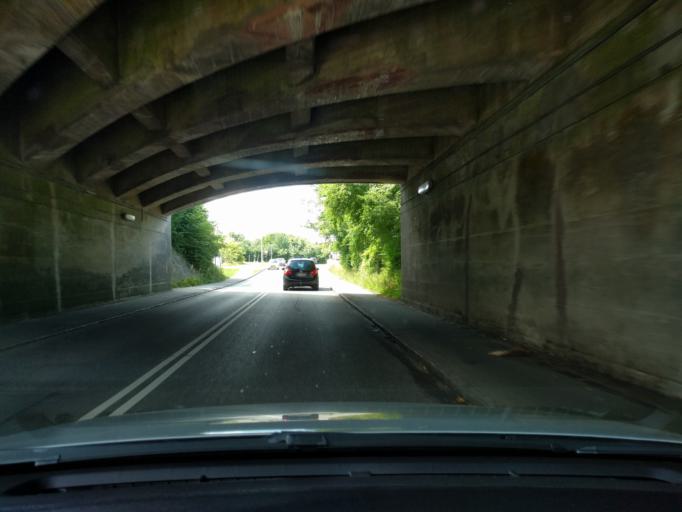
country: DK
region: South Denmark
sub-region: Fredericia Kommune
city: Snoghoj
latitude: 55.5257
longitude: 9.7160
